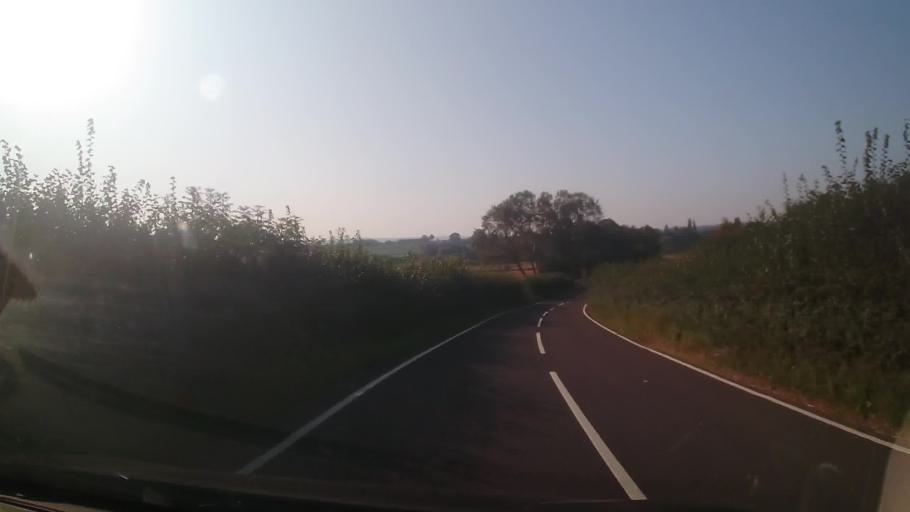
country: GB
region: England
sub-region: Shropshire
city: Harley
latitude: 52.6392
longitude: -2.5976
